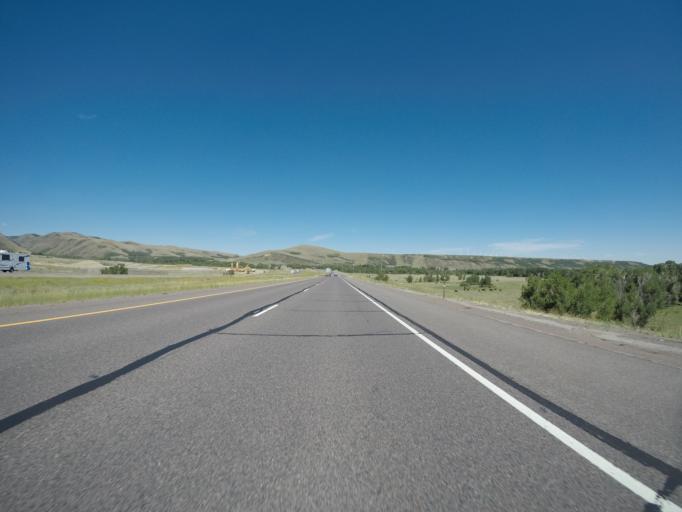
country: US
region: Wyoming
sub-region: Carbon County
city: Saratoga
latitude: 41.5952
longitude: -106.1941
